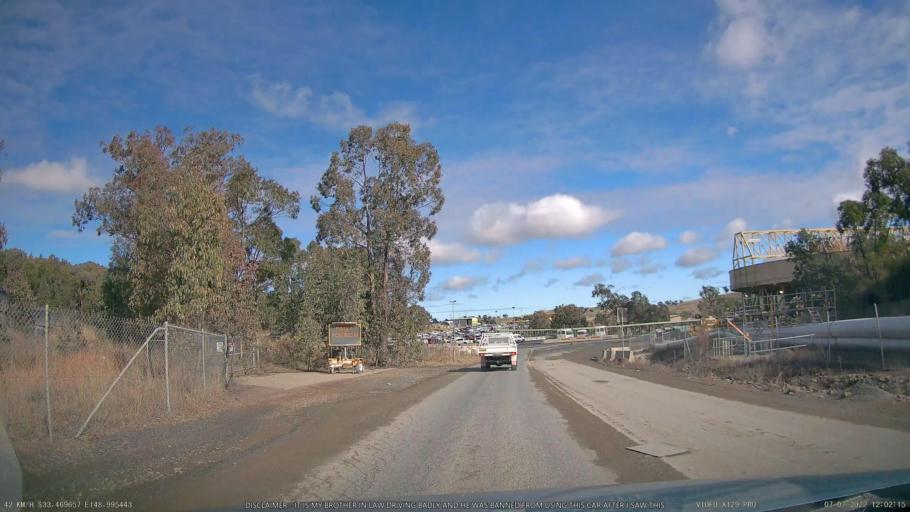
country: AU
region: New South Wales
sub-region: Blayney
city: Millthorpe
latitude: -33.4697
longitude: 148.9951
